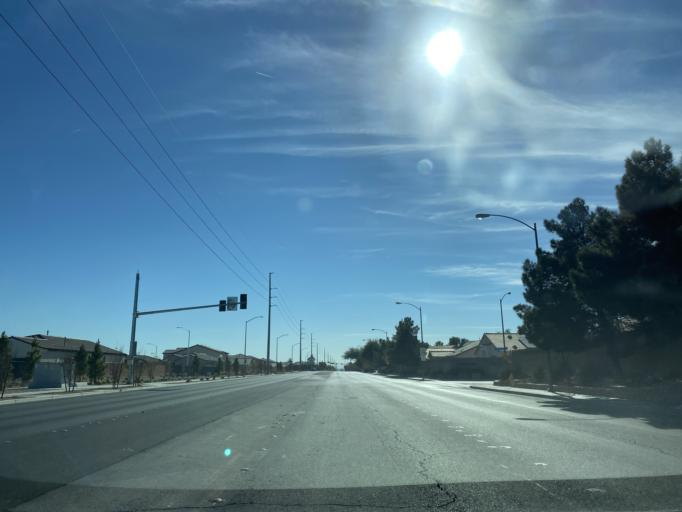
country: US
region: Nevada
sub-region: Clark County
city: North Las Vegas
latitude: 36.2650
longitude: -115.1440
